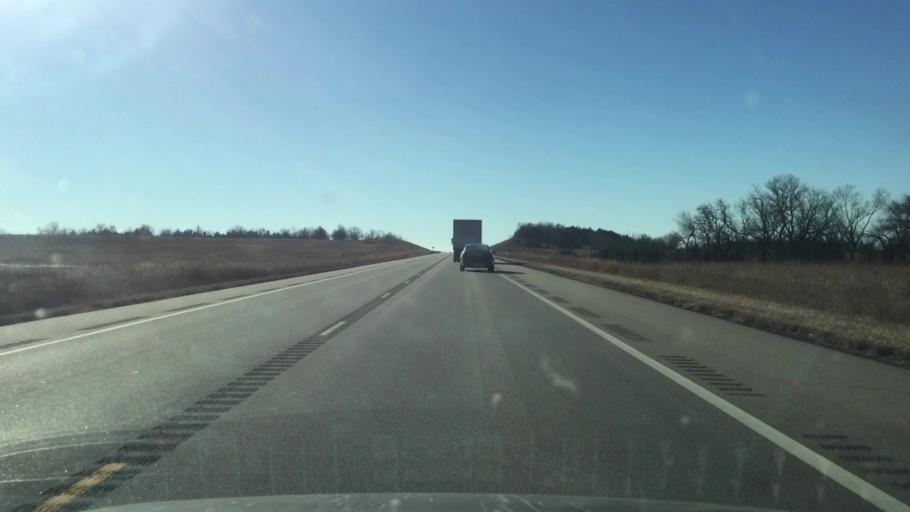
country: US
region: Kansas
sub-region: Allen County
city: Iola
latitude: 38.0179
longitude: -95.3807
